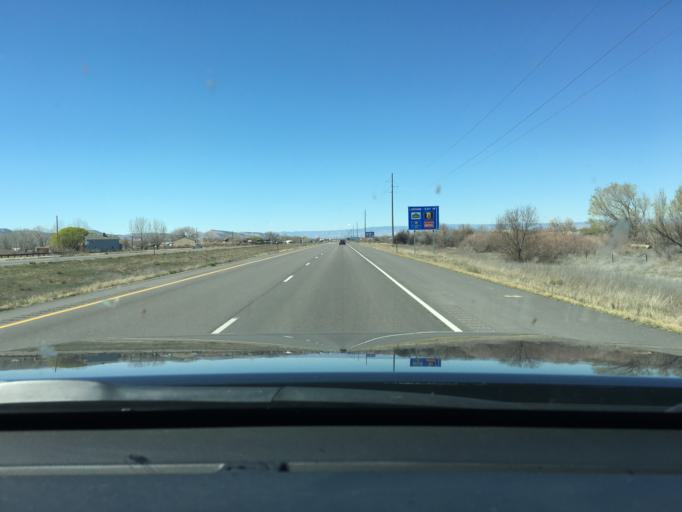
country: US
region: Colorado
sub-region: Mesa County
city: Fruita
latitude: 39.1424
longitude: -108.7099
